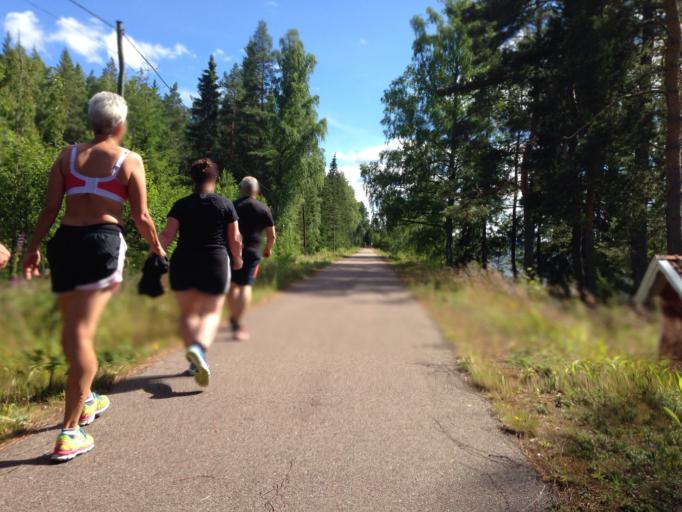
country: SE
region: Dalarna
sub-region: Ludvika Kommun
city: Grangesberg
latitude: 60.2271
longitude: 15.0332
